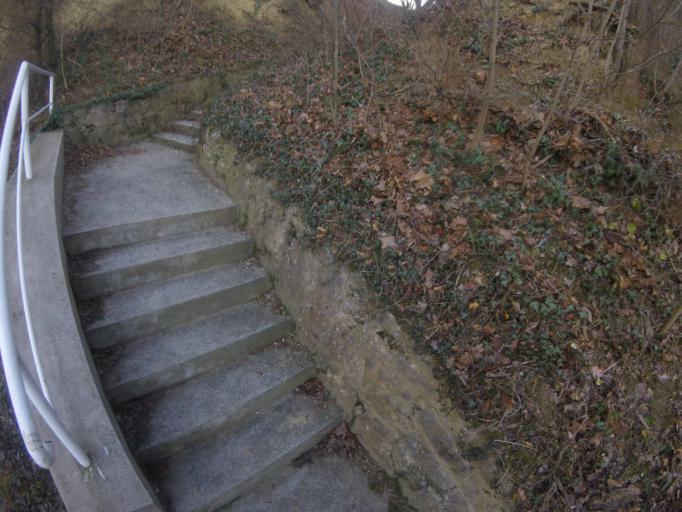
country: HU
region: Somogy
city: Balatonfoldvar
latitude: 46.8484
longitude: 17.8719
